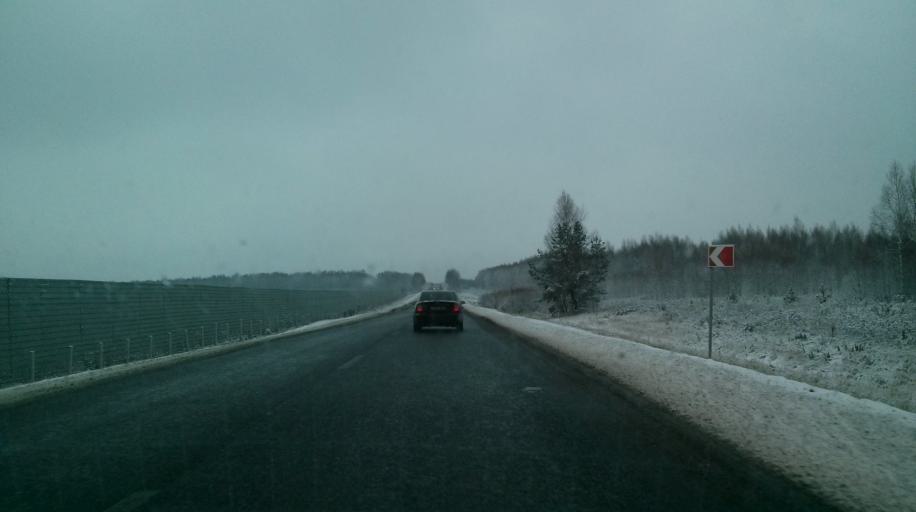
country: RU
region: Nizjnij Novgorod
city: Bogorodsk
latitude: 56.1211
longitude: 43.5956
